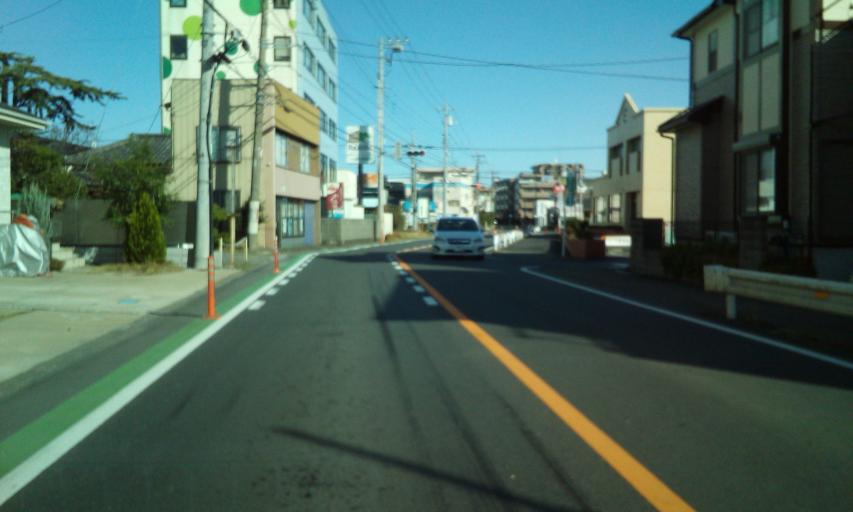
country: JP
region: Chiba
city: Nagareyama
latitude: 35.8501
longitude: 139.8816
